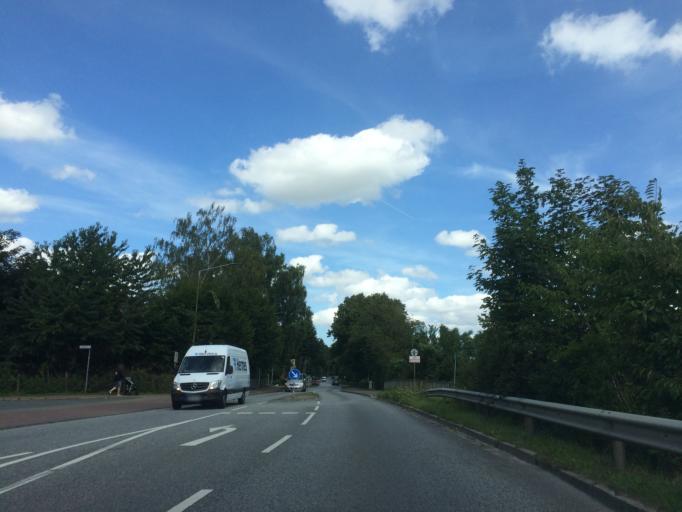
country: DE
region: Schleswig-Holstein
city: Ploen
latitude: 54.1625
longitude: 10.4282
